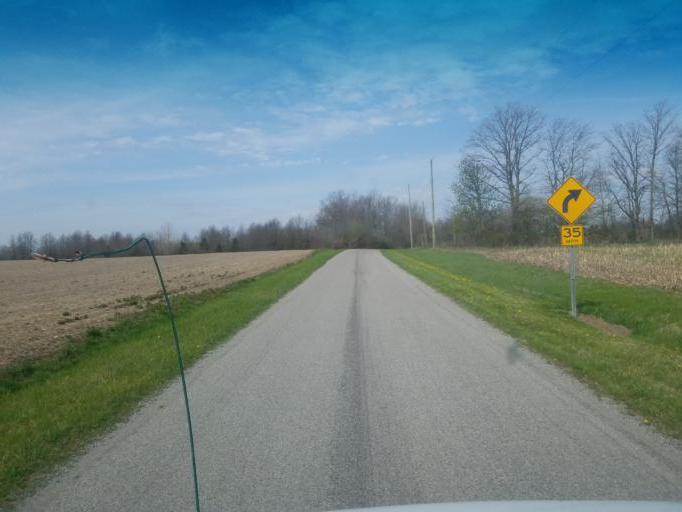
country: US
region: Ohio
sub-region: Union County
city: Richwood
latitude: 40.4814
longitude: -83.4375
